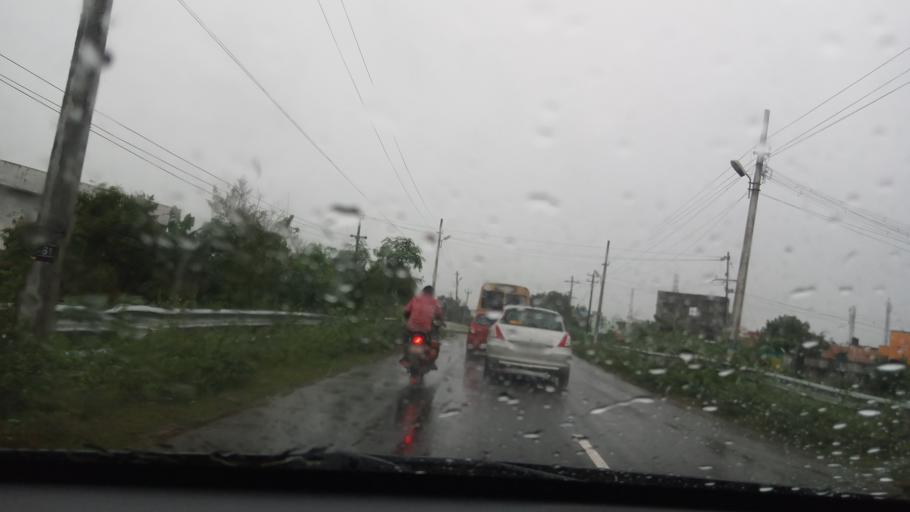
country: IN
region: Tamil Nadu
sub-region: Tiruvannamalai
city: Cheyyar
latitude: 12.6674
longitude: 79.5365
